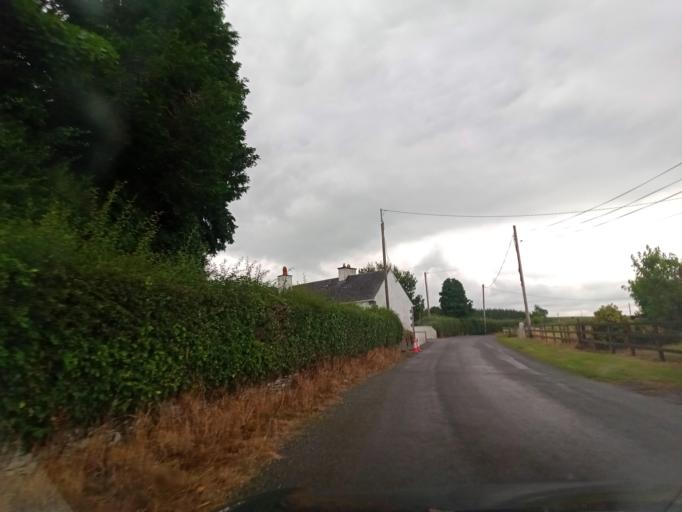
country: IE
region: Leinster
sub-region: Kilkenny
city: Castlecomer
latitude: 52.8958
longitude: -7.1457
